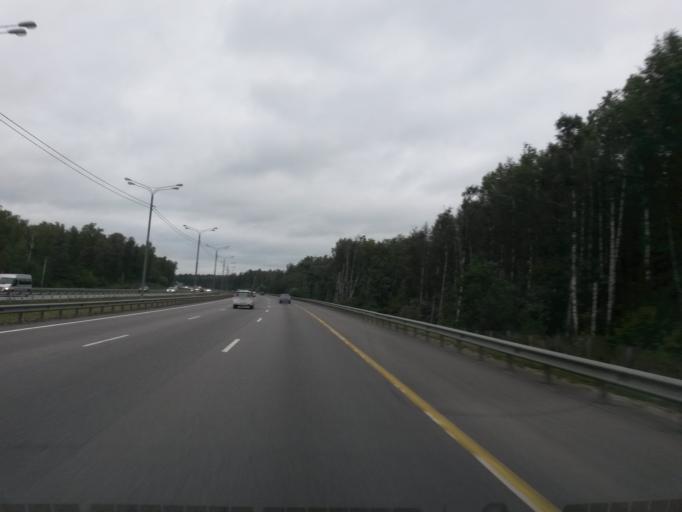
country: RU
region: Moskovskaya
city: Vostryakovo
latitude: 55.3536
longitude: 37.8038
